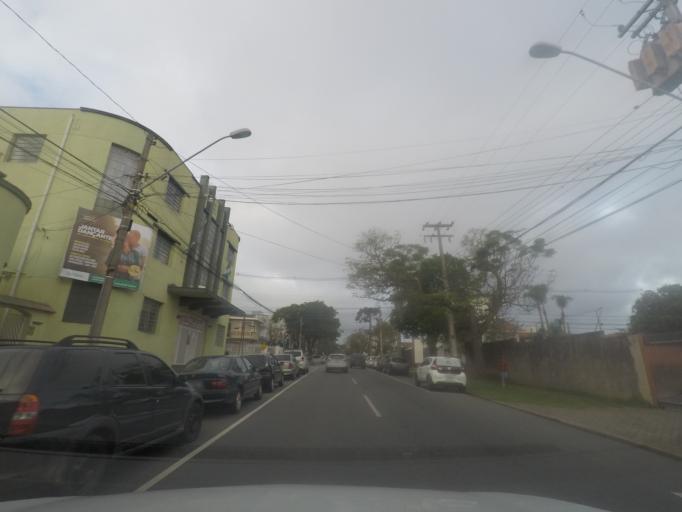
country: BR
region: Parana
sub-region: Curitiba
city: Curitiba
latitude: -25.4313
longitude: -49.2485
